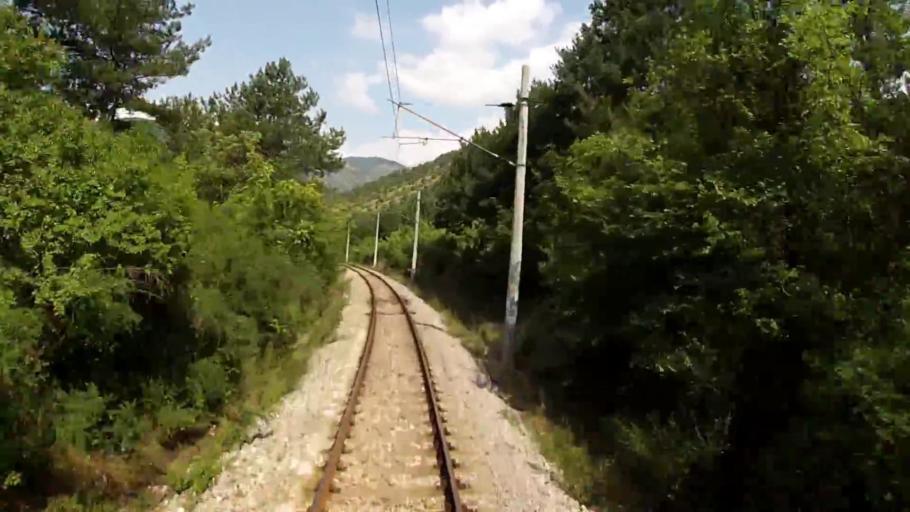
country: BG
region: Blagoevgrad
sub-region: Obshtina Kresna
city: Kresna
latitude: 41.7258
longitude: 23.1518
